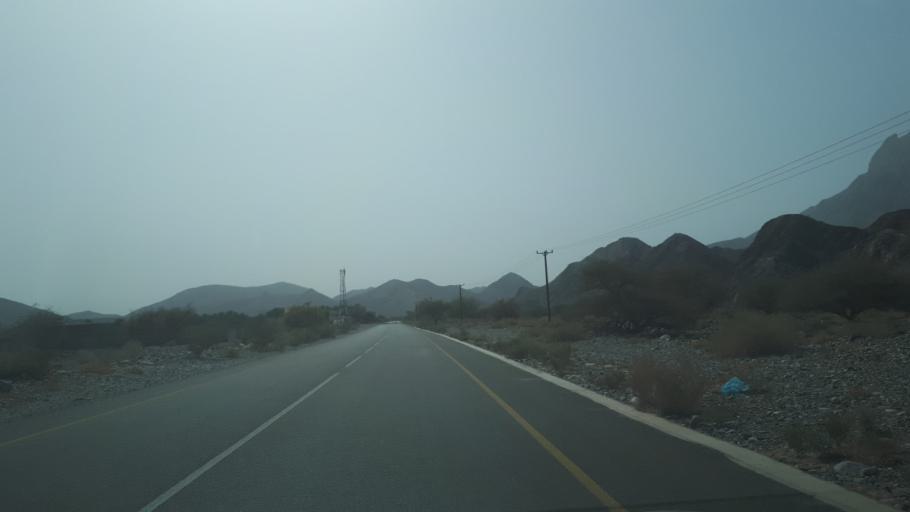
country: OM
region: Muhafazat ad Dakhiliyah
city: Bahla'
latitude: 23.2193
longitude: 57.0041
